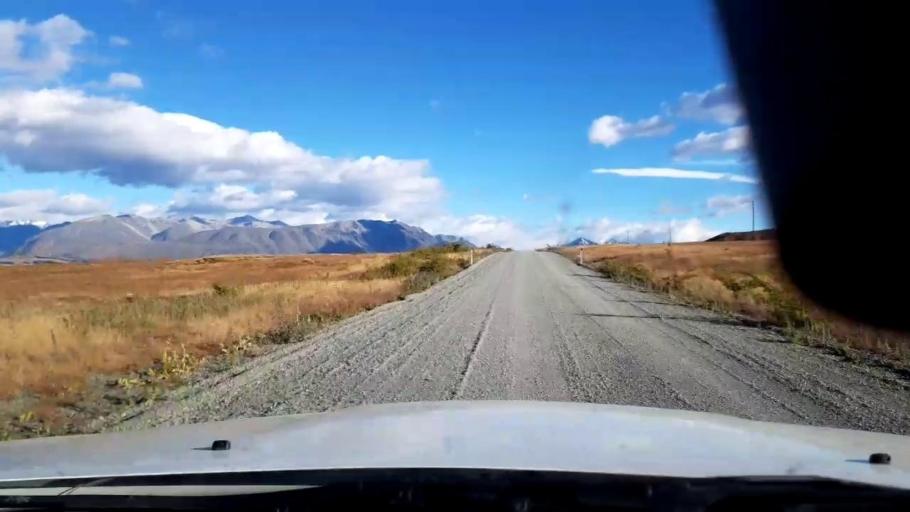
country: NZ
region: Canterbury
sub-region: Timaru District
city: Pleasant Point
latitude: -43.9232
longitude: 170.5597
